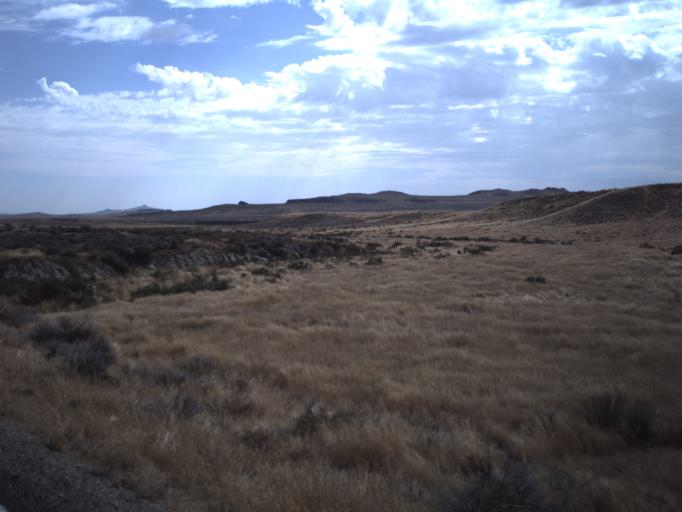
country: US
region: Nevada
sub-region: Elko County
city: West Wendover
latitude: 41.3723
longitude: -114.0249
